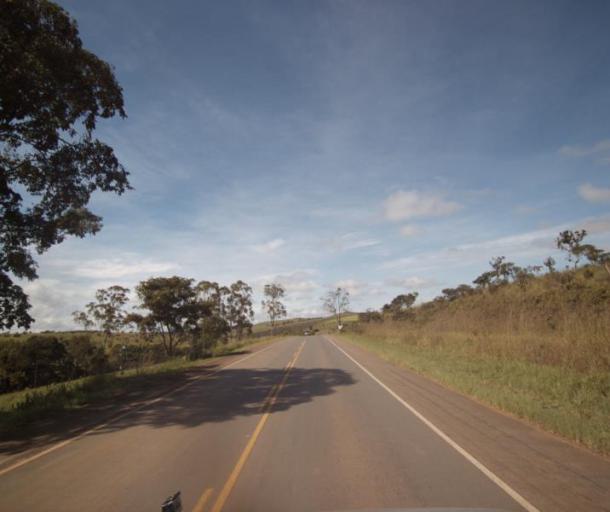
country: BR
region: Goias
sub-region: Anapolis
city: Anapolis
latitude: -16.1516
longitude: -48.8892
